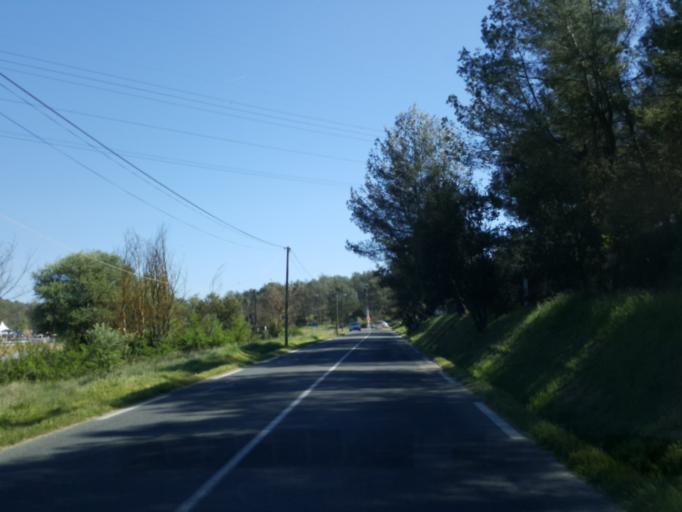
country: FR
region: Provence-Alpes-Cote d'Azur
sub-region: Departement des Bouches-du-Rhone
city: Cabries
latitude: 43.4576
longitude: 5.3540
